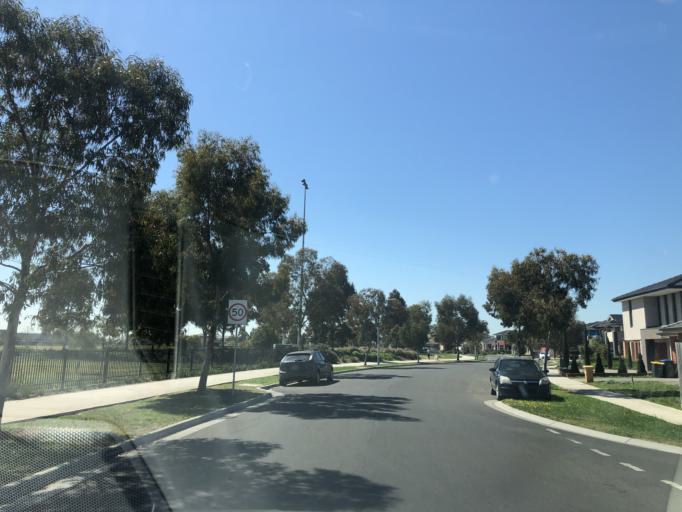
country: AU
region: Victoria
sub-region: Wyndham
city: Point Cook
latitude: -37.9012
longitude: 144.7304
